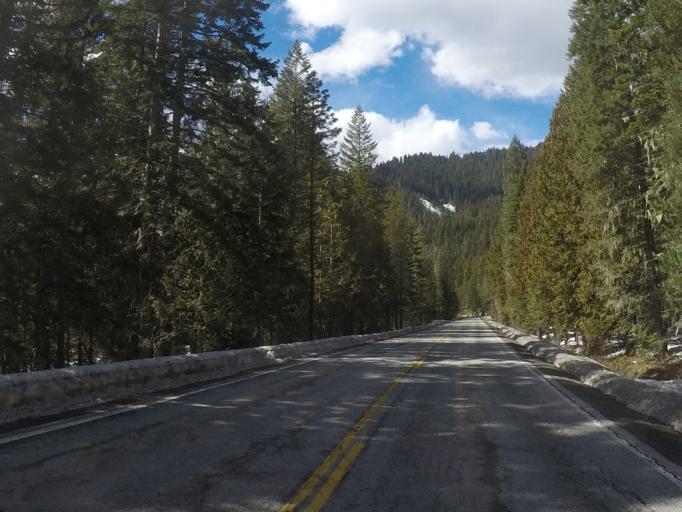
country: US
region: Montana
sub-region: Mineral County
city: Superior
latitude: 46.4765
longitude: -114.8768
